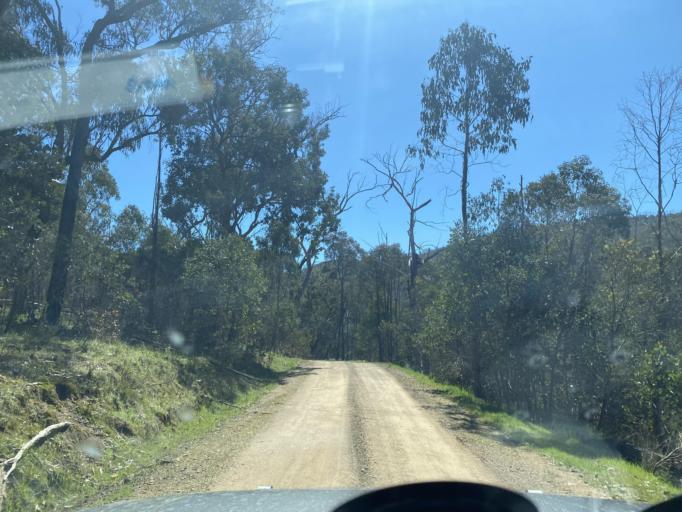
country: AU
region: Victoria
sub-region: Benalla
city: Benalla
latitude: -36.7046
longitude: 146.1780
